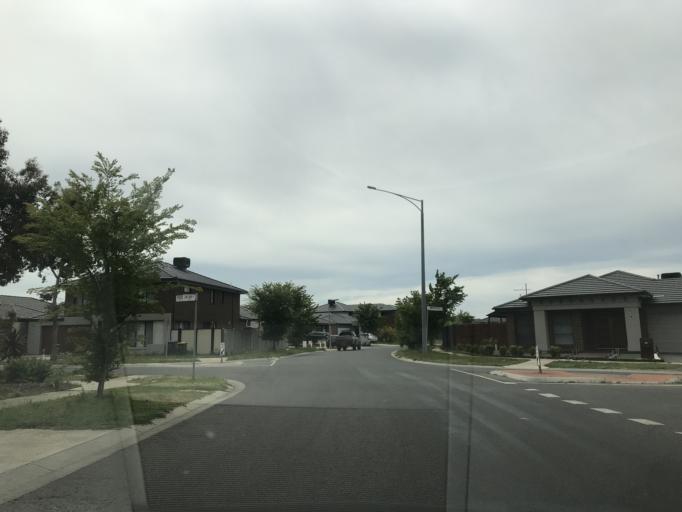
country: AU
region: Victoria
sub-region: Wyndham
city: Tarneit
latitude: -37.8384
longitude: 144.6840
